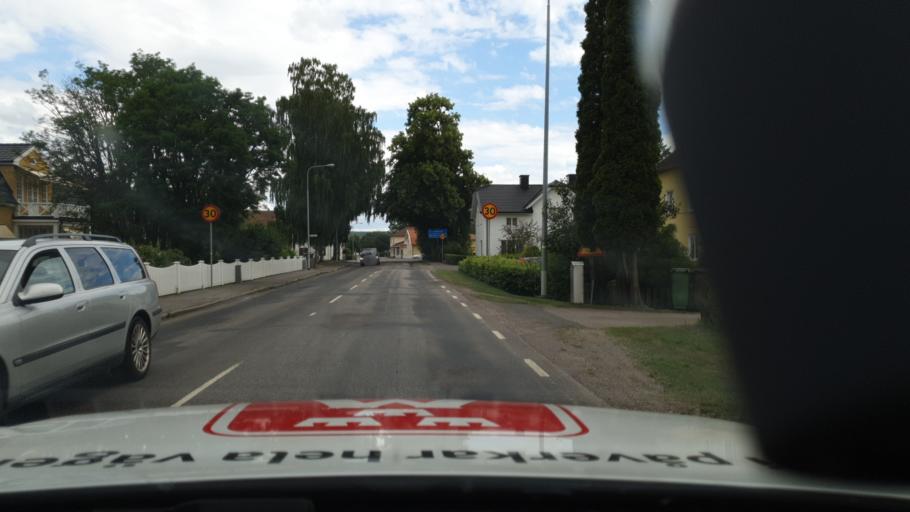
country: SE
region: Vaestra Goetaland
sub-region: Skara Kommun
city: Axvall
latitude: 58.3896
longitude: 13.5714
